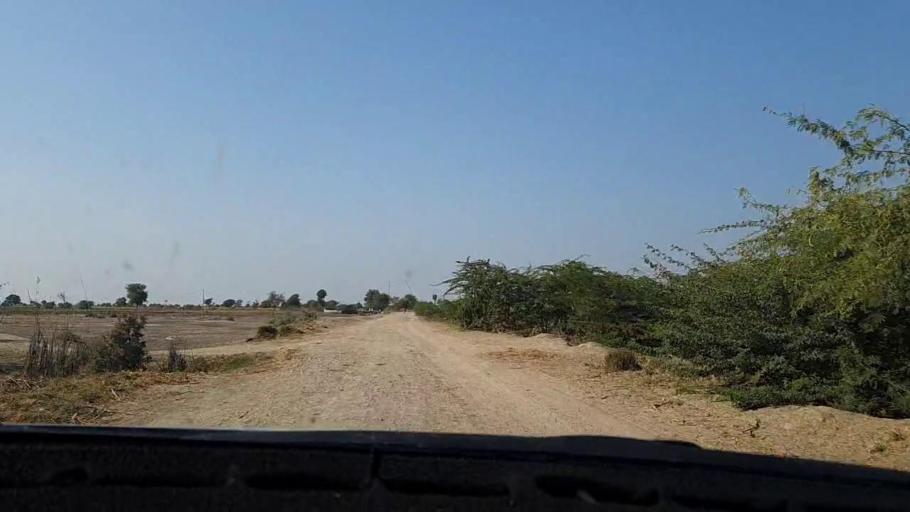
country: PK
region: Sindh
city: Tando Mittha Khan
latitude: 25.8138
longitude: 69.2905
